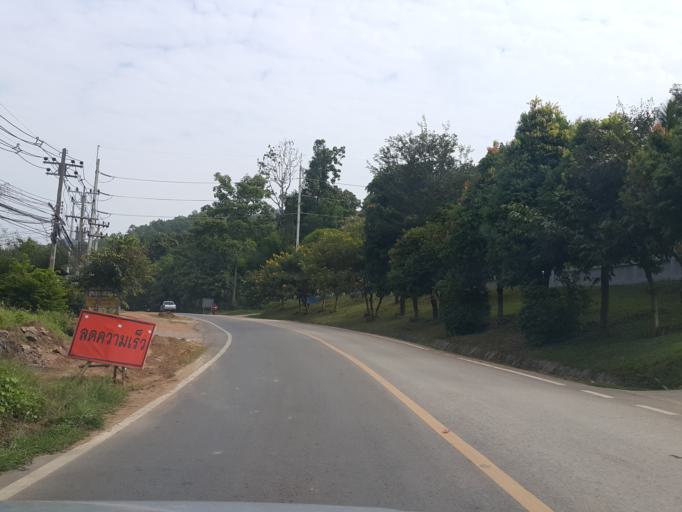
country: TH
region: Mae Hong Son
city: Mae Hong Son
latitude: 19.3151
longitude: 97.9652
